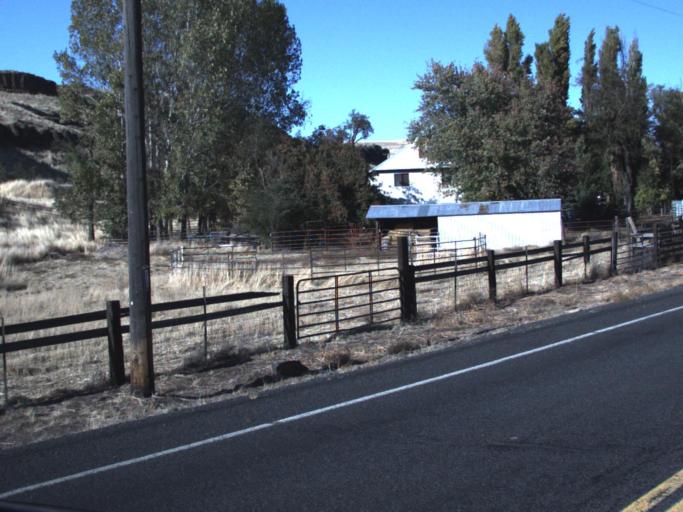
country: US
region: Washington
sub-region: Adams County
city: Ritzville
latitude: 46.7475
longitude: -118.3182
